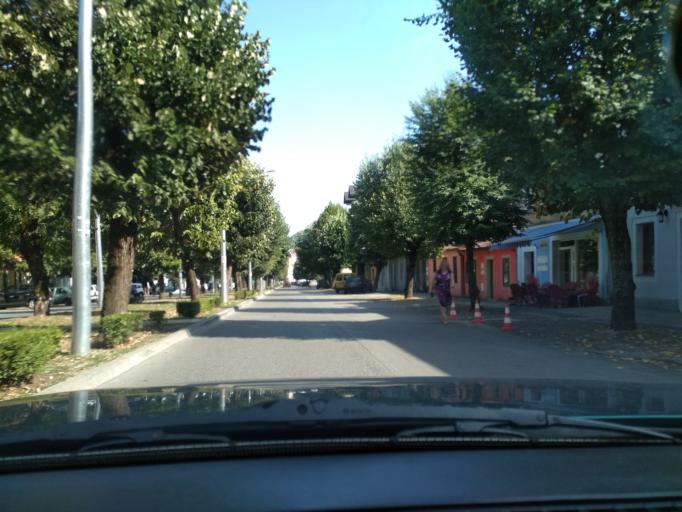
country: ME
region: Cetinje
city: Cetinje
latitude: 42.3933
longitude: 18.9186
